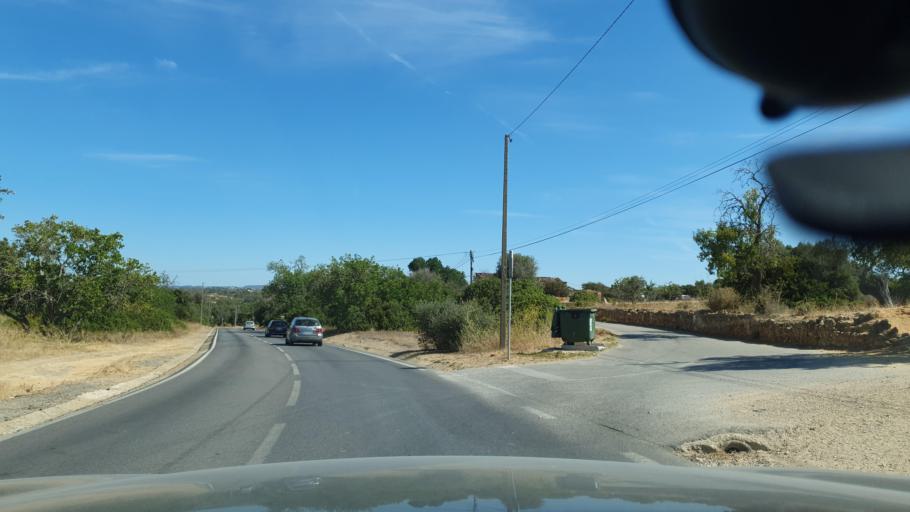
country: PT
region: Faro
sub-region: Albufeira
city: Guia
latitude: 37.1029
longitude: -8.3078
